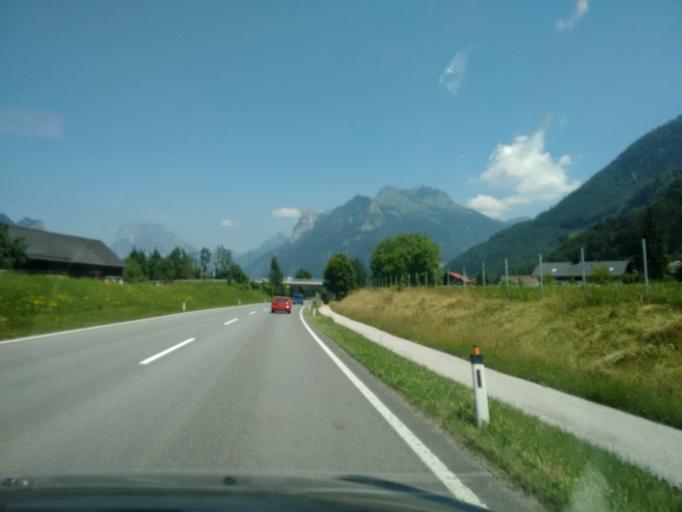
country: AT
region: Upper Austria
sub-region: Politischer Bezirk Gmunden
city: Ebensee
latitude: 47.7916
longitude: 13.7642
